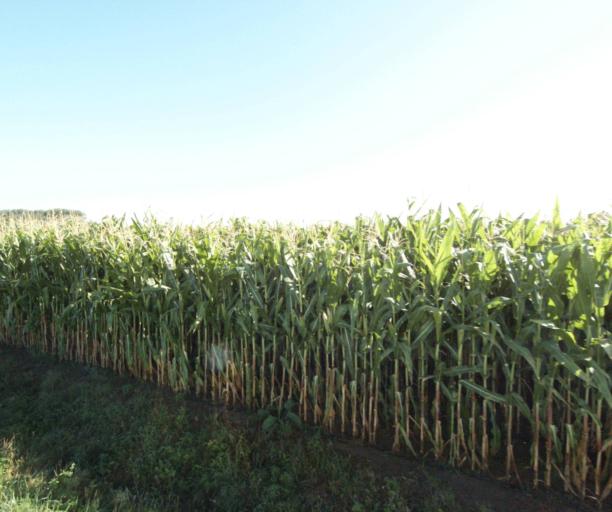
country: FR
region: Nord-Pas-de-Calais
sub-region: Departement du Nord
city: Toufflers
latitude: 50.6476
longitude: 3.2336
